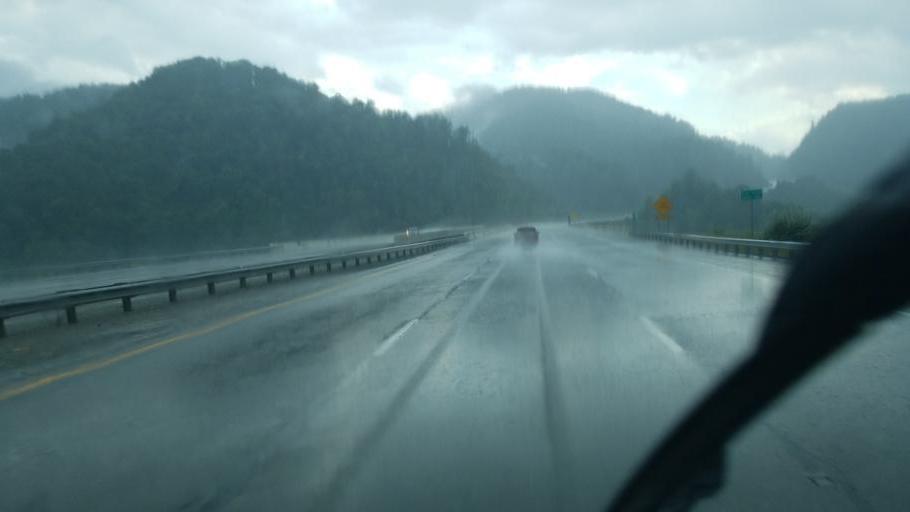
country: US
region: Kentucky
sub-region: Pike County
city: Pikeville
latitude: 37.5603
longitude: -82.4226
